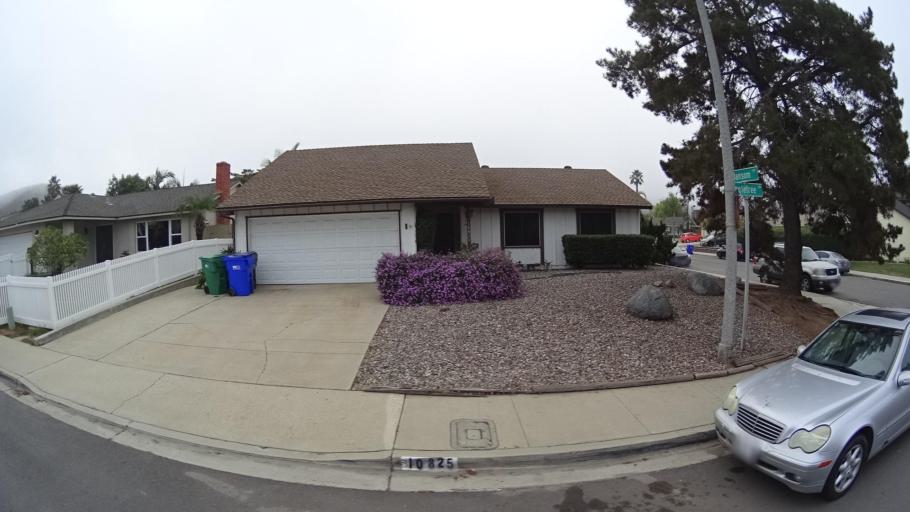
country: US
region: California
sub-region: San Diego County
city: Rancho San Diego
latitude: 32.7309
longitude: -116.9595
